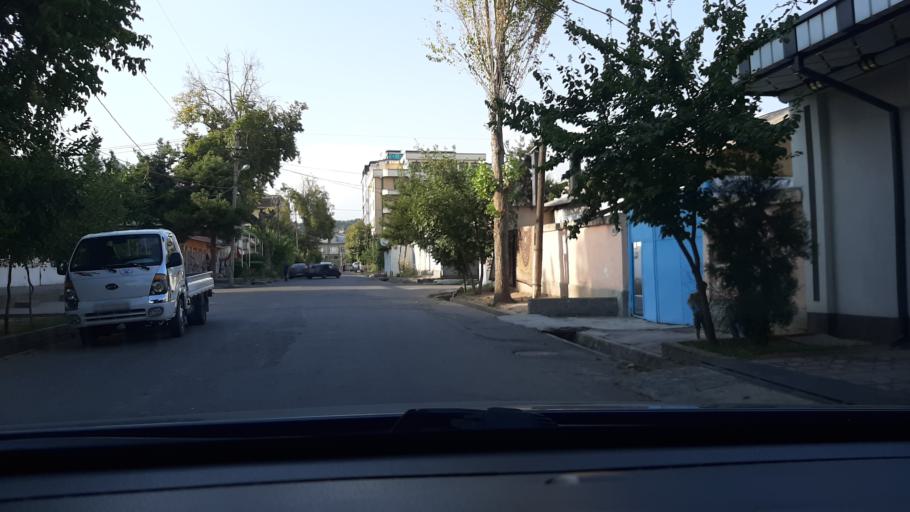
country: TJ
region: Dushanbe
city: Dushanbe
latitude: 38.5652
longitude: 68.8117
